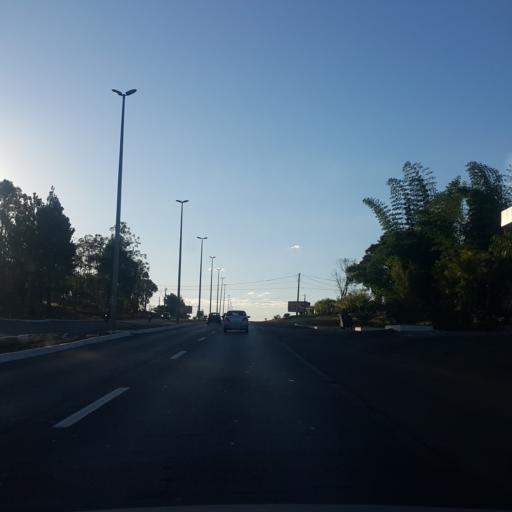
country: BR
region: Federal District
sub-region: Brasilia
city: Brasilia
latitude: -15.8597
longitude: -47.9872
